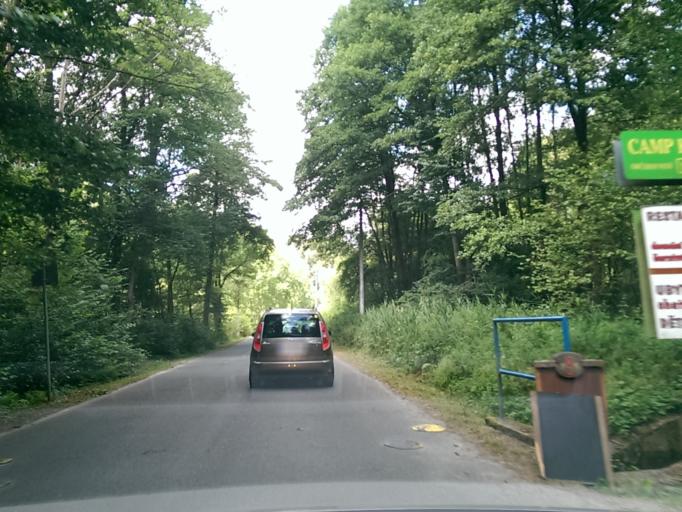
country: CZ
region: Central Bohemia
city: Mseno
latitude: 50.4347
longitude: 14.5816
